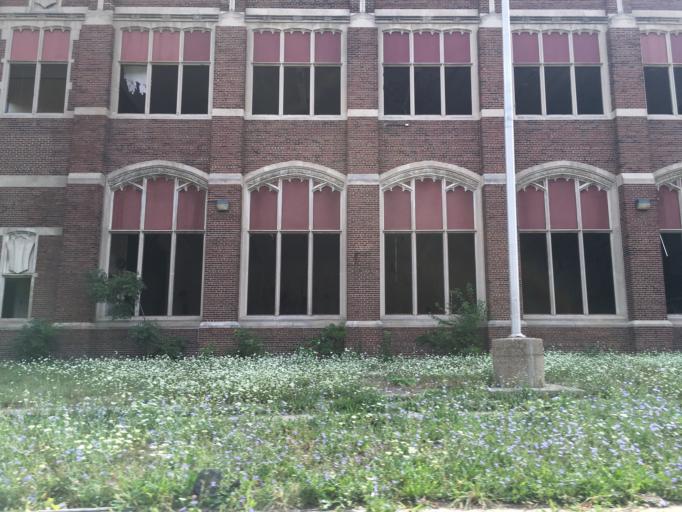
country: US
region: Michigan
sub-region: Wayne County
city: Highland Park
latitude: 42.3750
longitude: -83.0949
